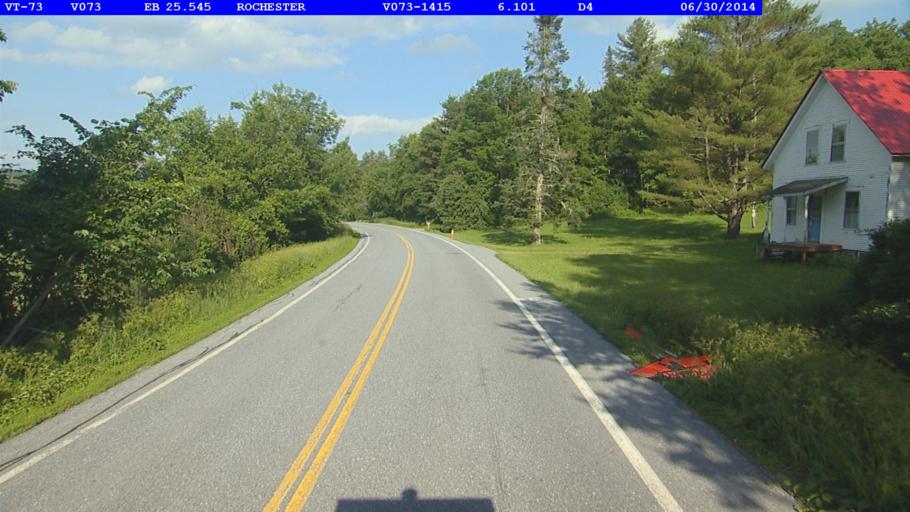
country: US
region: Vermont
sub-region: Orange County
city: Randolph
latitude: 43.8480
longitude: -72.8547
